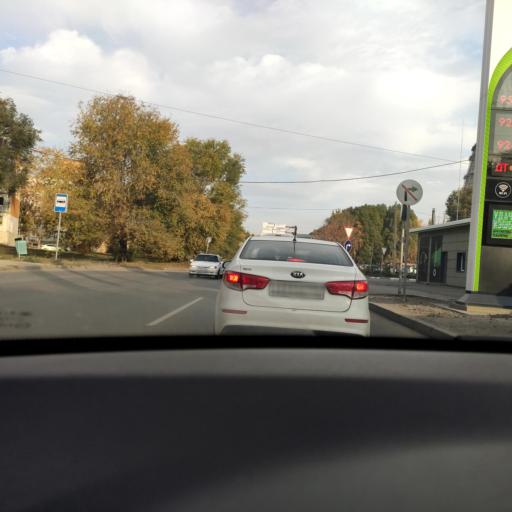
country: RU
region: Samara
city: Petra-Dubrava
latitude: 53.2470
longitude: 50.2693
